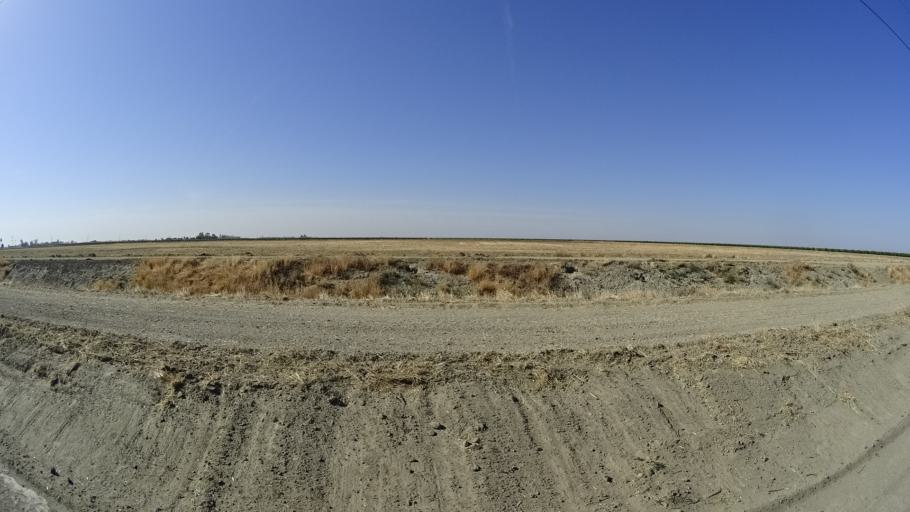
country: US
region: California
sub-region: Kings County
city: Corcoran
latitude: 36.0835
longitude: -119.5791
